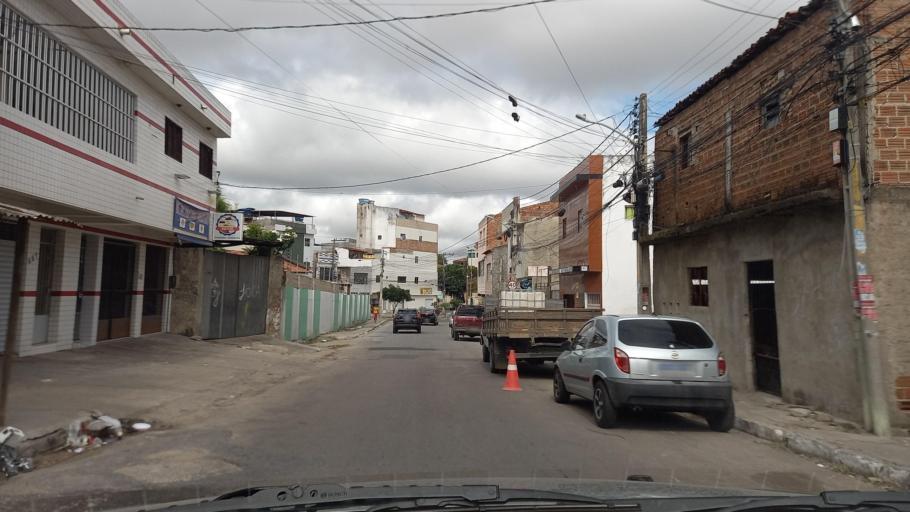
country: BR
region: Pernambuco
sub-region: Caruaru
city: Caruaru
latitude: -8.2817
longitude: -35.9797
